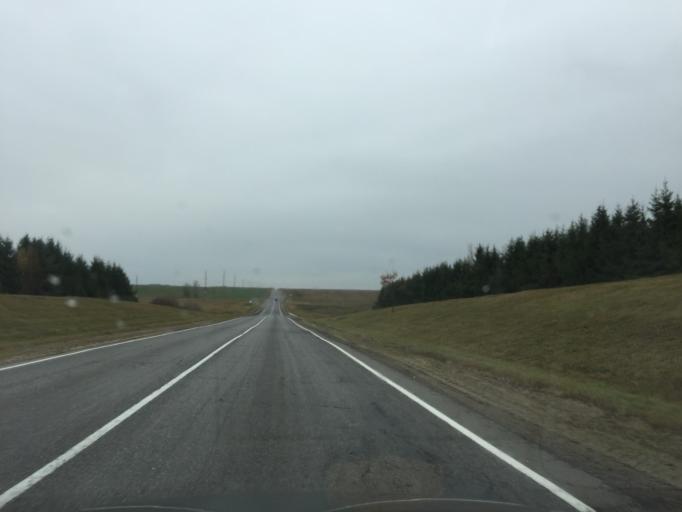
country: BY
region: Mogilev
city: Cherykaw
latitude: 53.6314
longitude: 31.2861
